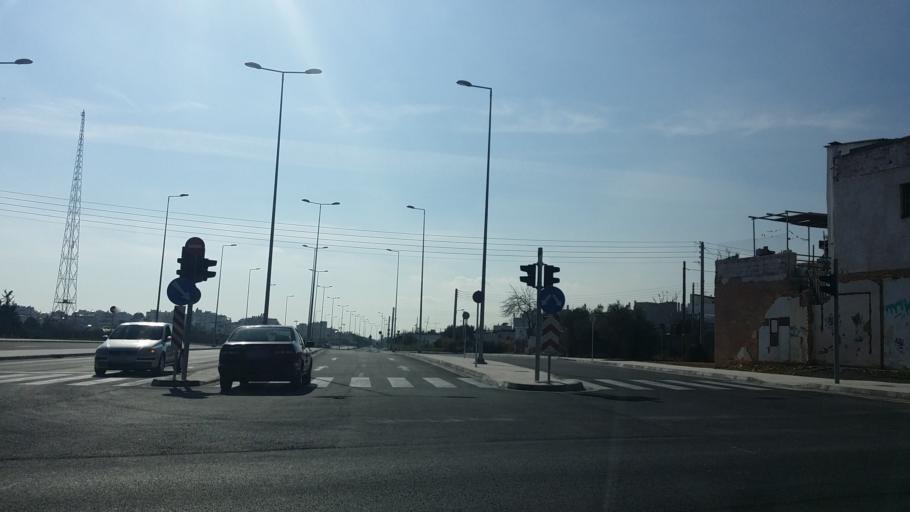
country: GR
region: Attica
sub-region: Nomarchia Athinas
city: Kamateron
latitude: 38.0432
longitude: 23.7105
